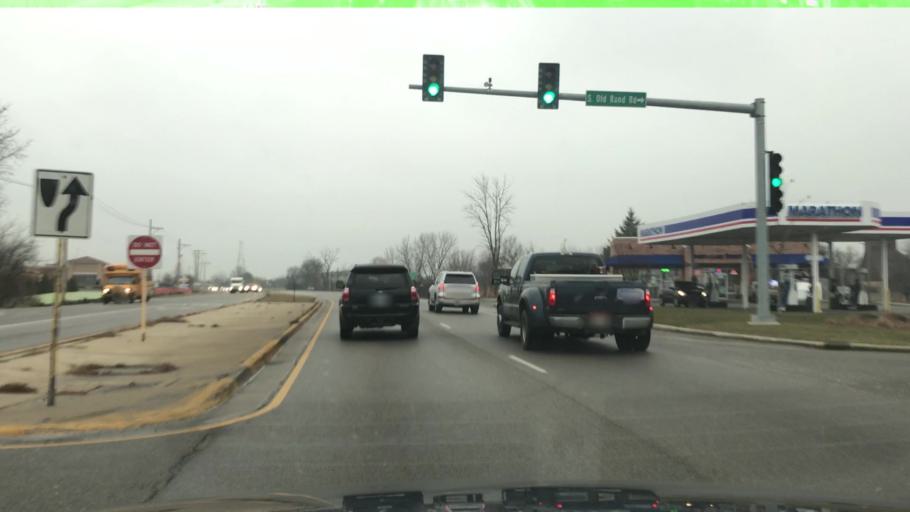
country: US
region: Illinois
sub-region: Lake County
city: Deer Park
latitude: 42.1792
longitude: -88.0778
